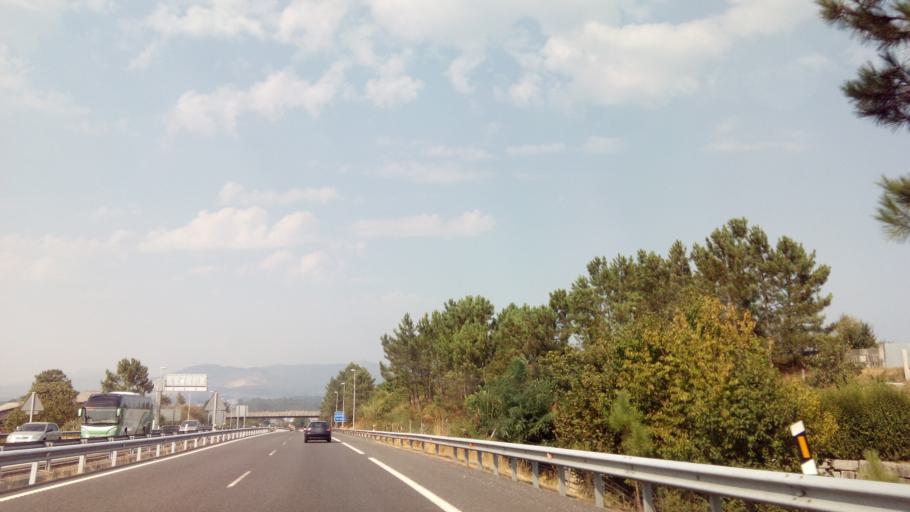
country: ES
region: Galicia
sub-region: Provincia de Pontevedra
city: Tui
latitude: 42.0810
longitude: -8.6301
